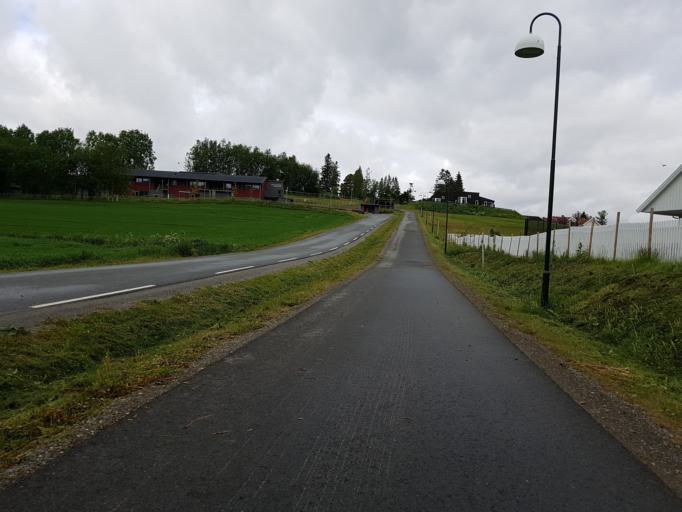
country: NO
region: Sor-Trondelag
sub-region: Selbu
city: Mebonden
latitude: 63.2210
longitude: 11.0336
